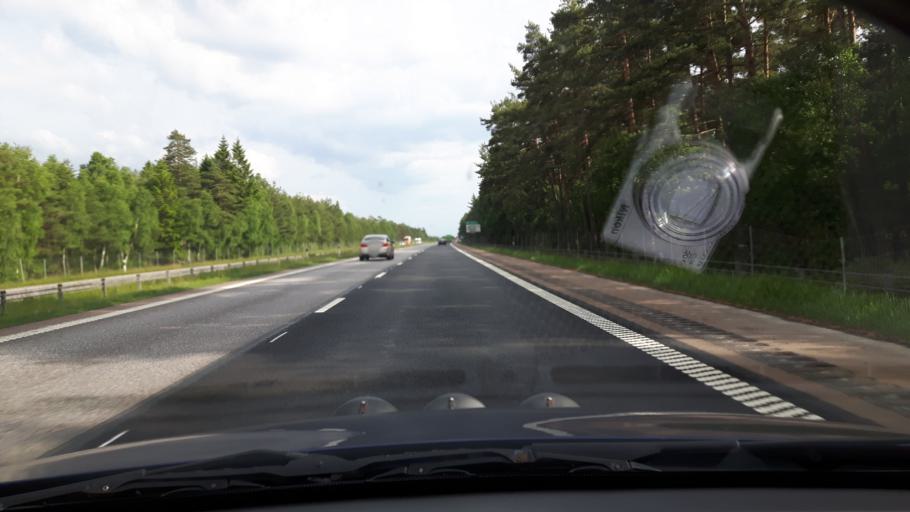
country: SE
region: Halland
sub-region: Laholms Kommun
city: Mellbystrand
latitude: 56.5548
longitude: 12.9613
